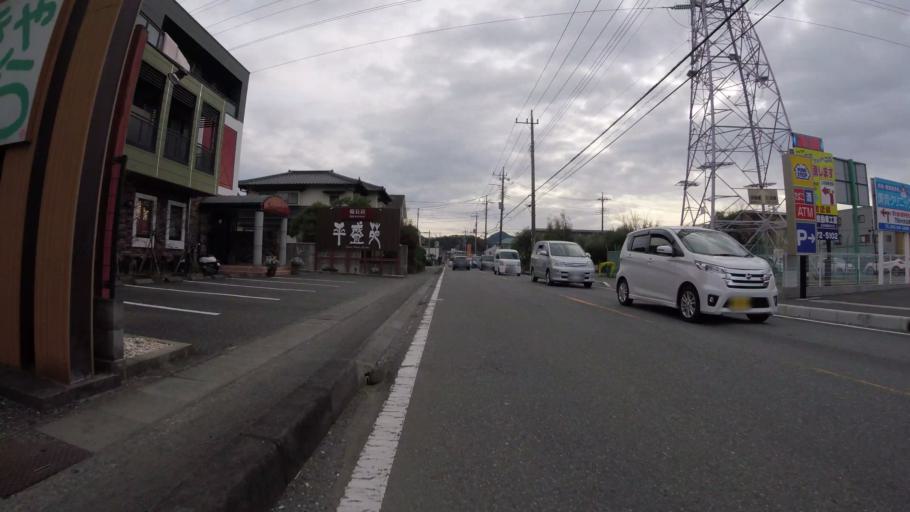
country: JP
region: Shizuoka
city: Mishima
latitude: 35.1041
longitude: 138.8986
